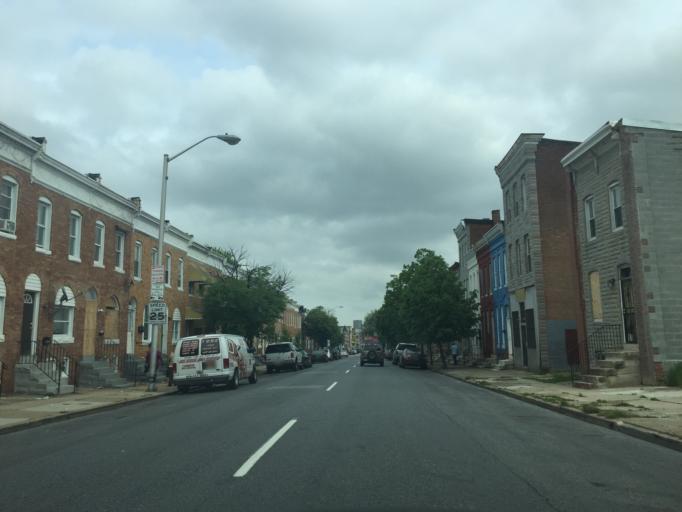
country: US
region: Maryland
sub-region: City of Baltimore
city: Baltimore
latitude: 39.3128
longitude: -76.6406
